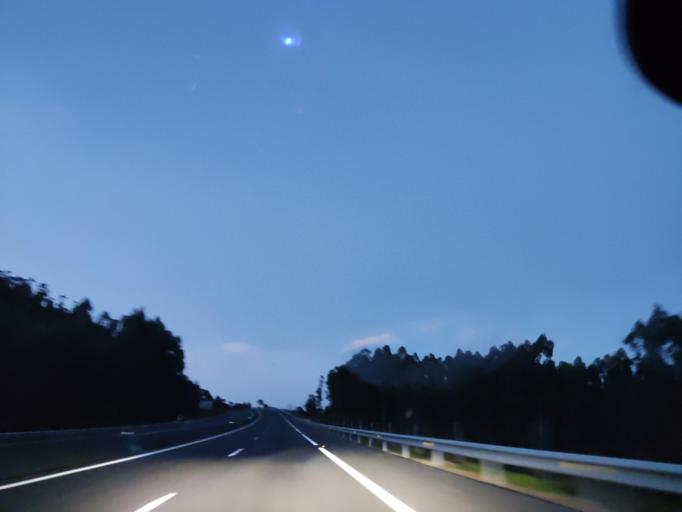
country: ES
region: Galicia
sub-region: Provincia de Pontevedra
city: Catoira
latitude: 42.6728
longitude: -8.7708
